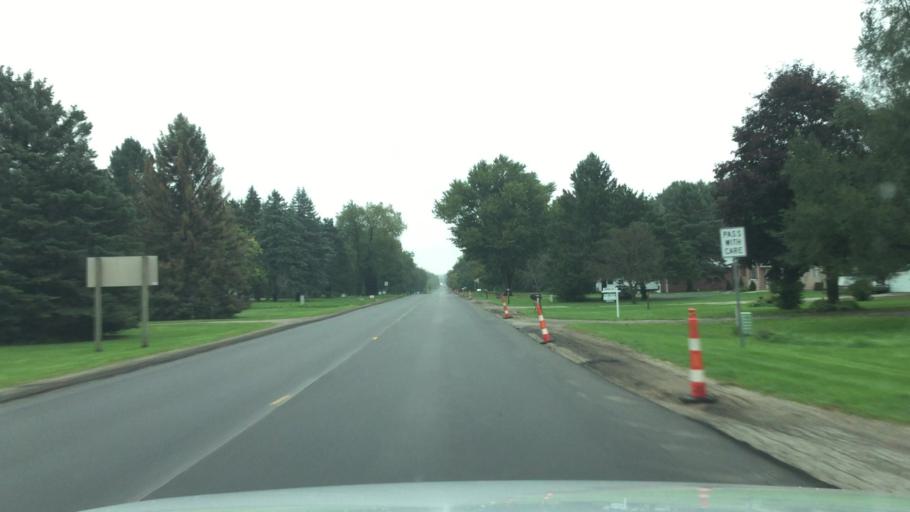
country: US
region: Michigan
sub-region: Shiawassee County
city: Perry
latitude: 42.8905
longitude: -84.2219
